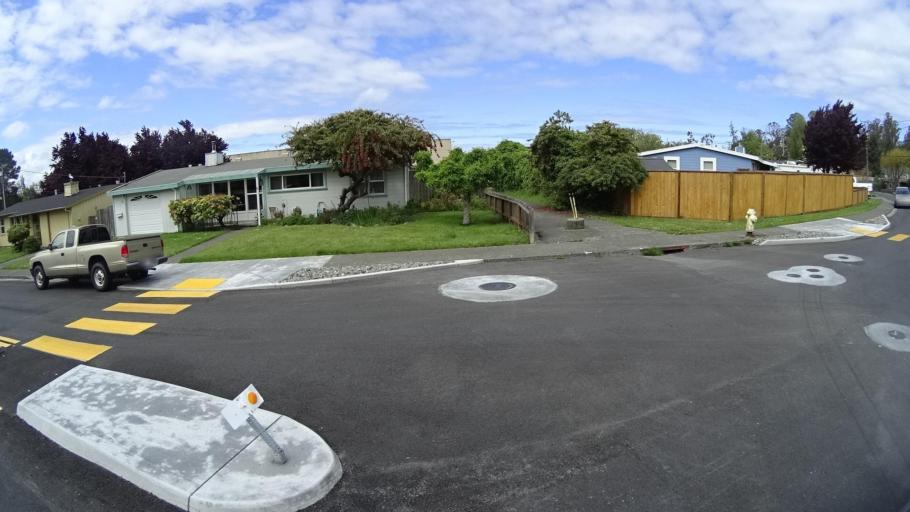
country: US
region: California
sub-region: Humboldt County
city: Arcata
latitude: 40.8582
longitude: -124.0705
